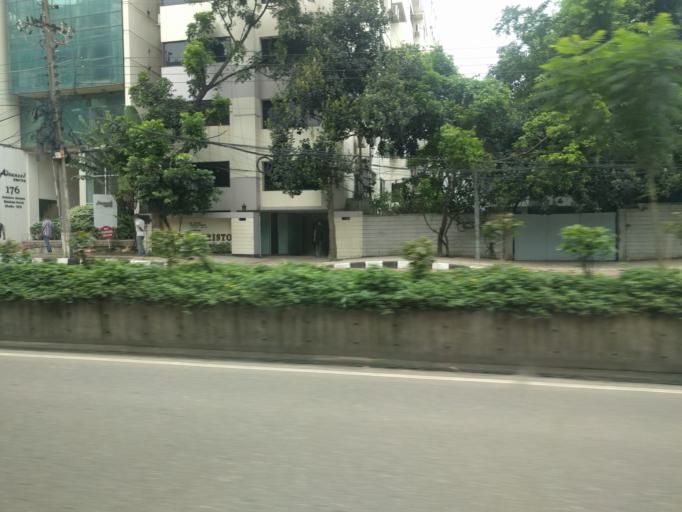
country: BD
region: Dhaka
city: Paltan
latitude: 23.7983
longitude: 90.4127
